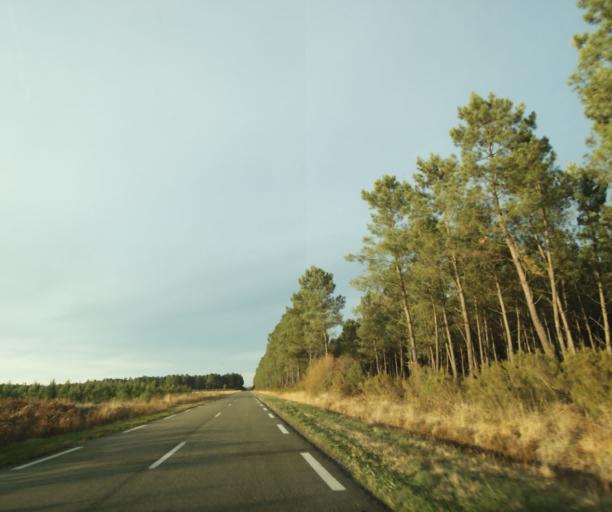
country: FR
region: Aquitaine
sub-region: Departement des Landes
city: Roquefort
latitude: 44.1732
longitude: -0.1412
